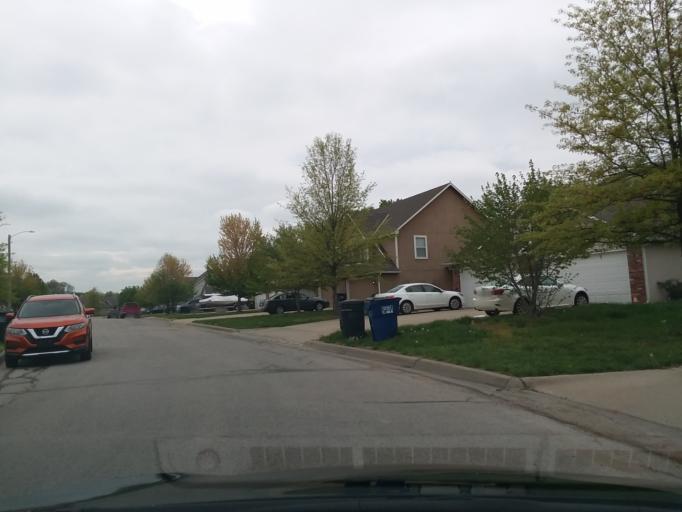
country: US
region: Kansas
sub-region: Douglas County
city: Lawrence
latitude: 38.9942
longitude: -95.2800
